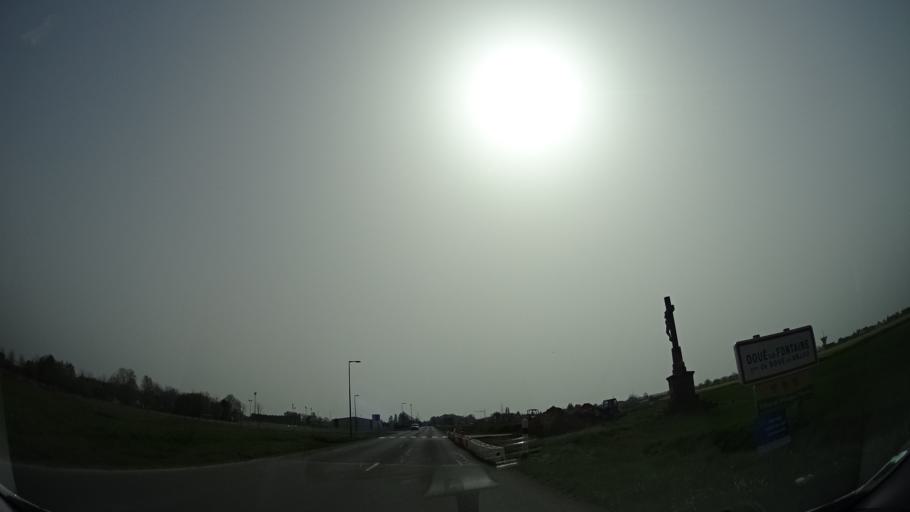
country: FR
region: Pays de la Loire
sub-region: Departement de Maine-et-Loire
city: Doue-la-Fontaine
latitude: 47.2036
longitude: -0.2874
